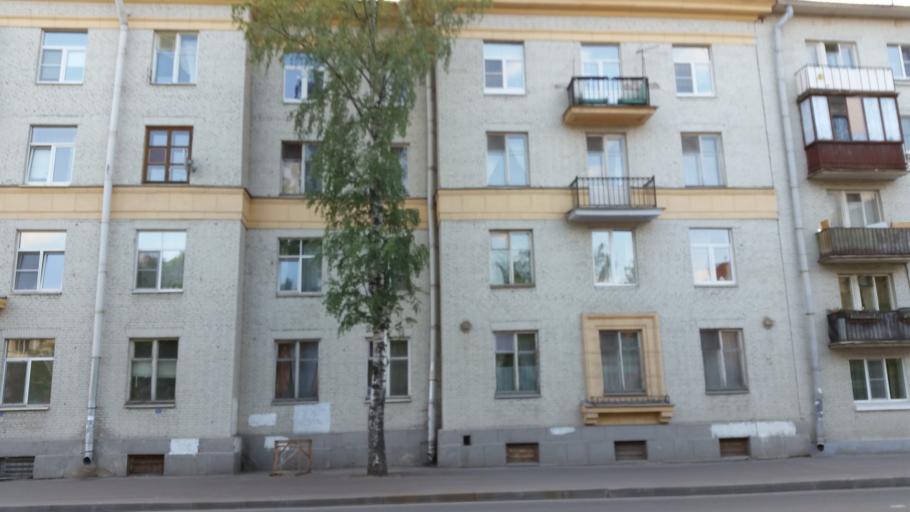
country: RU
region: St.-Petersburg
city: Sosnovaya Polyana
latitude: 59.8434
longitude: 30.1471
